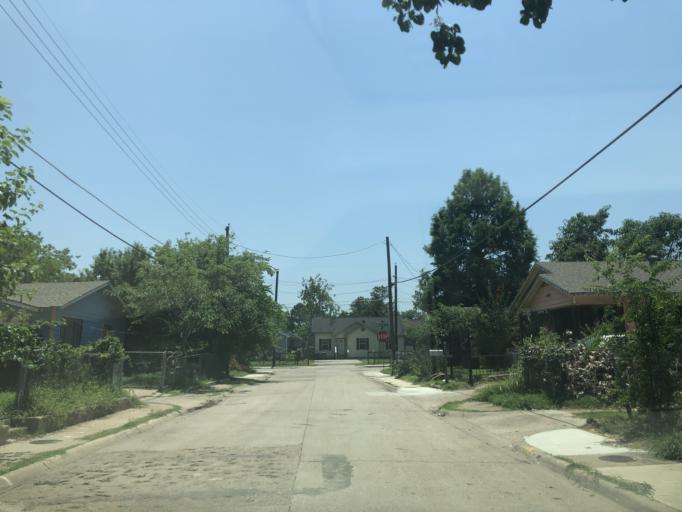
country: US
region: Texas
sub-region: Dallas County
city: Dallas
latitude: 32.7839
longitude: -96.8430
